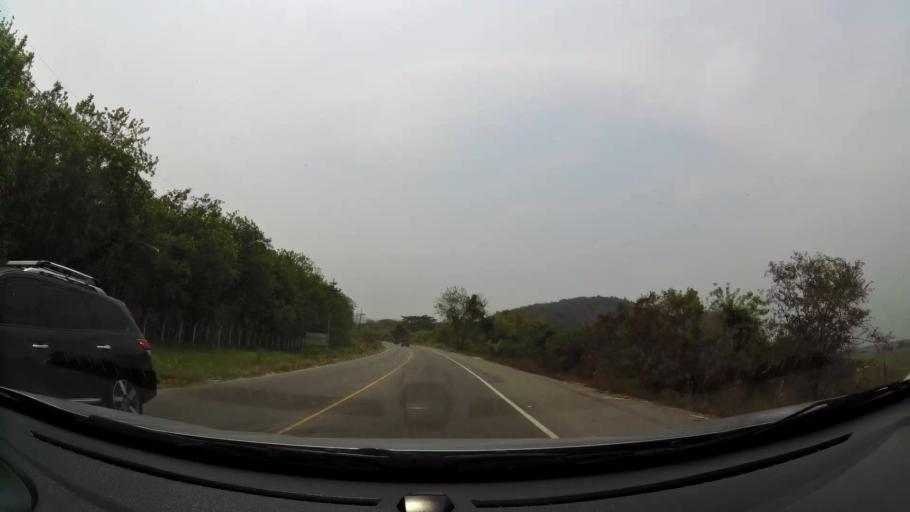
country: HN
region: Cortes
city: Bejuco
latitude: 15.1682
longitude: -87.9504
